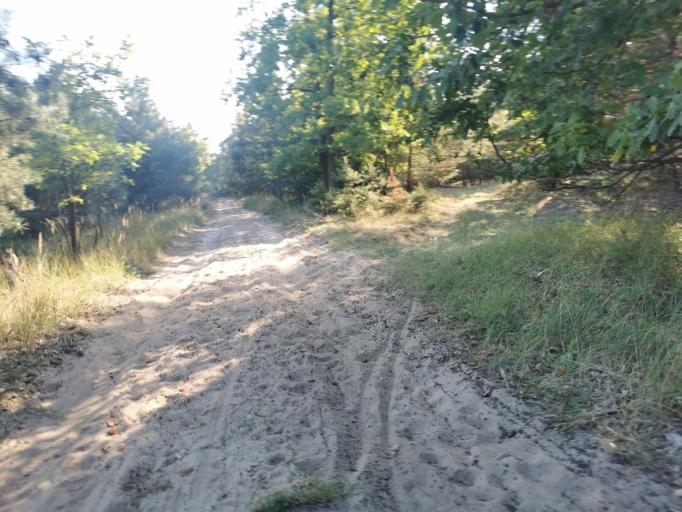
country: SK
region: Trnavsky
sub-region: Okres Senica
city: Senica
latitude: 48.6485
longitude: 17.2900
